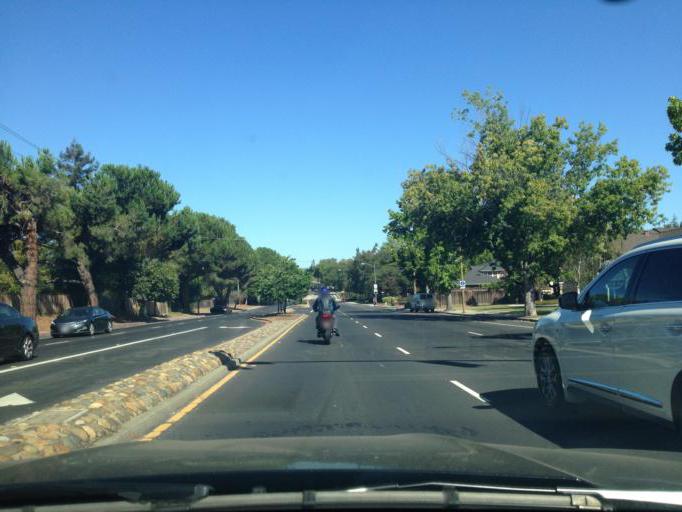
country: US
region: California
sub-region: Santa Clara County
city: Los Gatos
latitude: 37.2509
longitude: -121.9622
